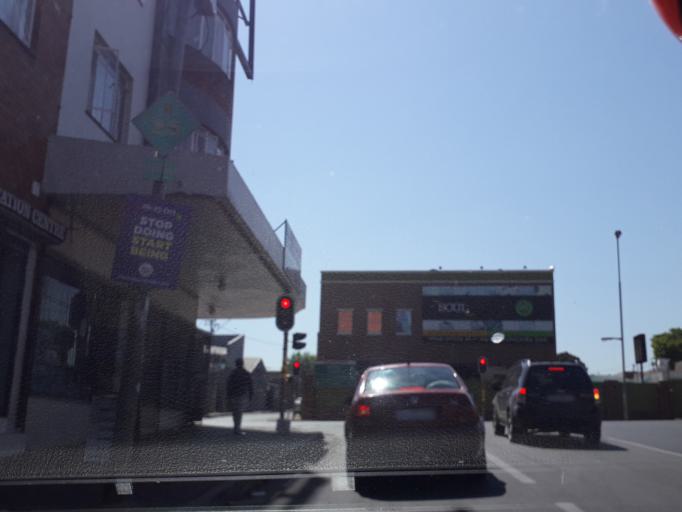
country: ZA
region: Gauteng
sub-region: City of Johannesburg Metropolitan Municipality
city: Johannesburg
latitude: -26.1573
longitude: 28.0850
